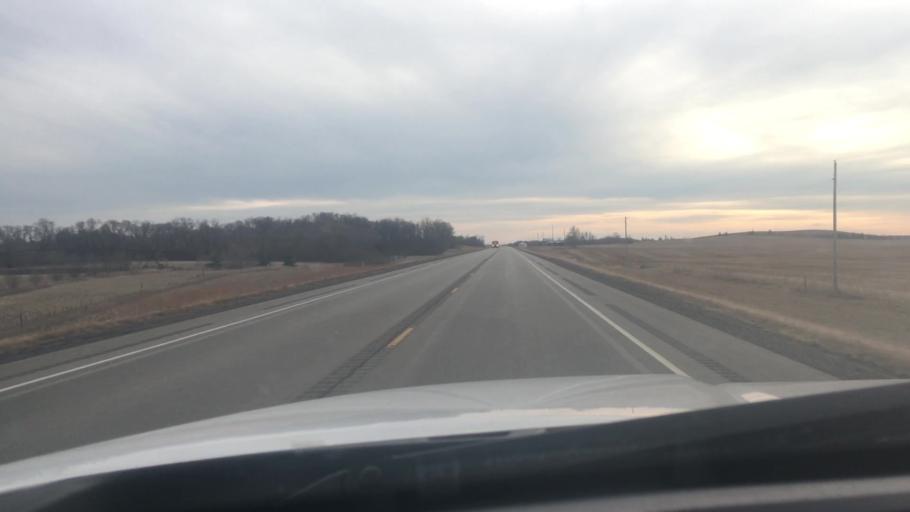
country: US
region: Minnesota
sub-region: Otter Tail County
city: Perham
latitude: 46.3330
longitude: -95.7185
